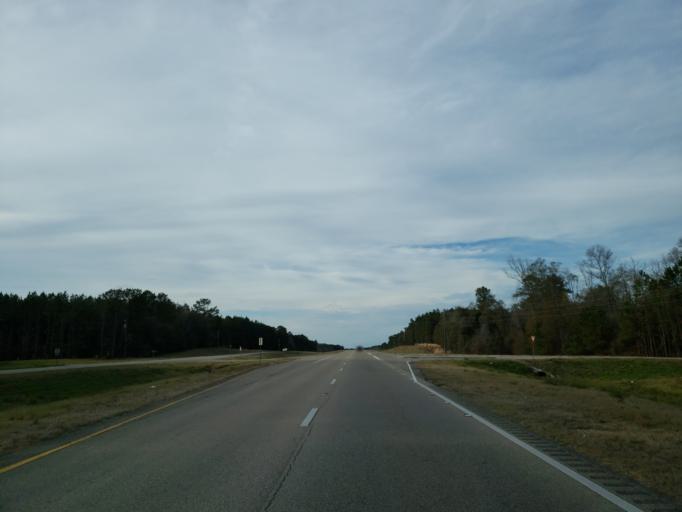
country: US
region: Mississippi
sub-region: Wayne County
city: Waynesboro
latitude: 31.6180
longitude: -88.5774
